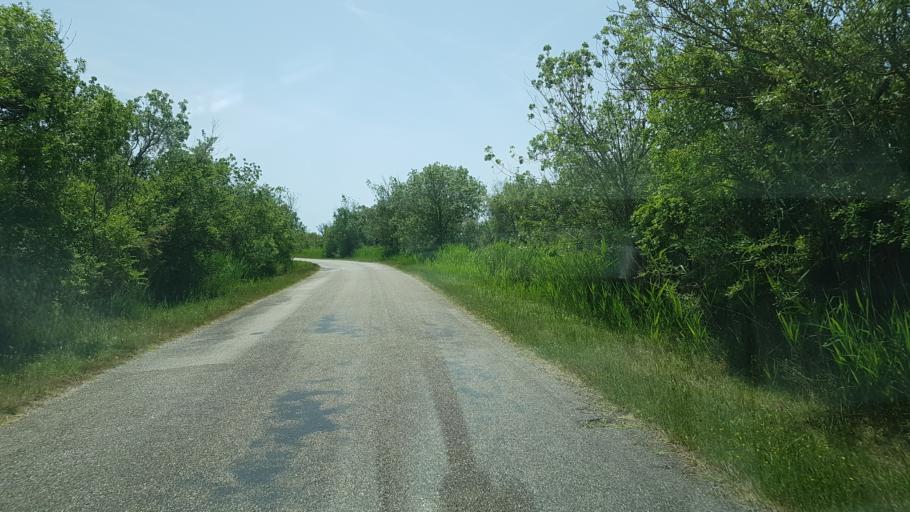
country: FR
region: Provence-Alpes-Cote d'Azur
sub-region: Departement des Bouches-du-Rhone
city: Port-Saint-Louis-du-Rhone
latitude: 43.4668
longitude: 4.6506
